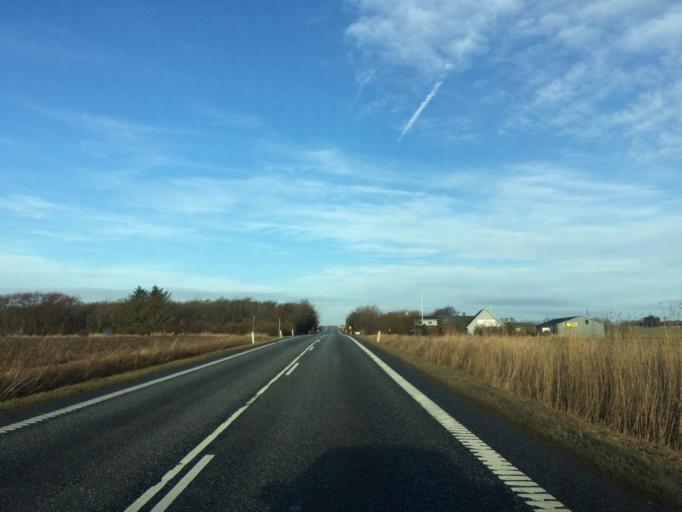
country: DK
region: North Denmark
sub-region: Thisted Kommune
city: Hurup
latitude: 56.6914
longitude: 8.4017
